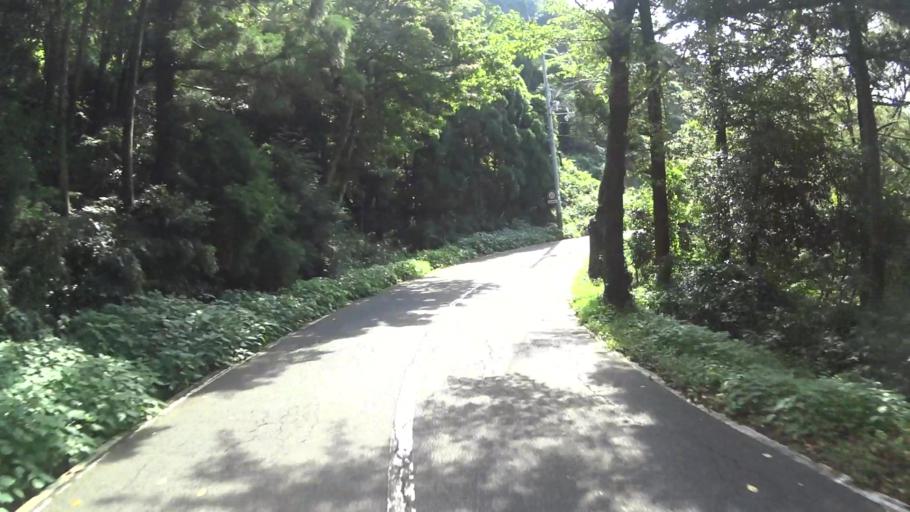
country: JP
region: Kyoto
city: Miyazu
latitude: 35.7696
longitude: 135.2221
